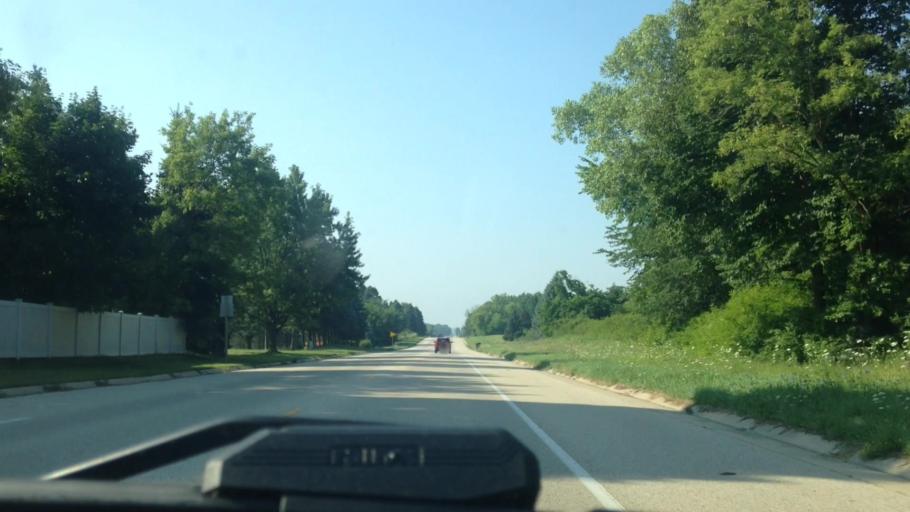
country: US
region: Wisconsin
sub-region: Washington County
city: Slinger
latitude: 43.3223
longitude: -88.2607
